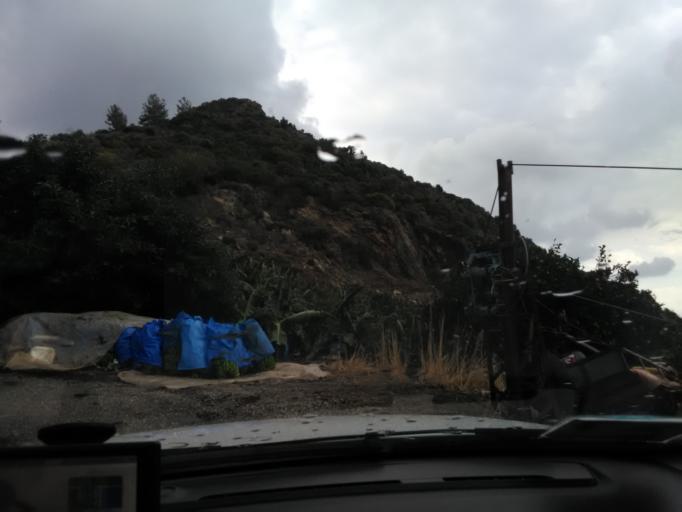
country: TR
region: Antalya
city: Gazipasa
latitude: 36.1565
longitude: 32.4190
